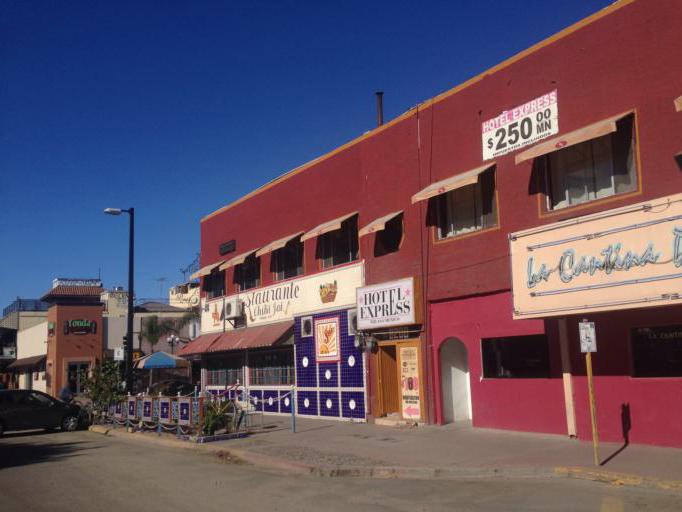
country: MX
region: Baja California
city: Tijuana
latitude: 32.5296
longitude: -117.0358
